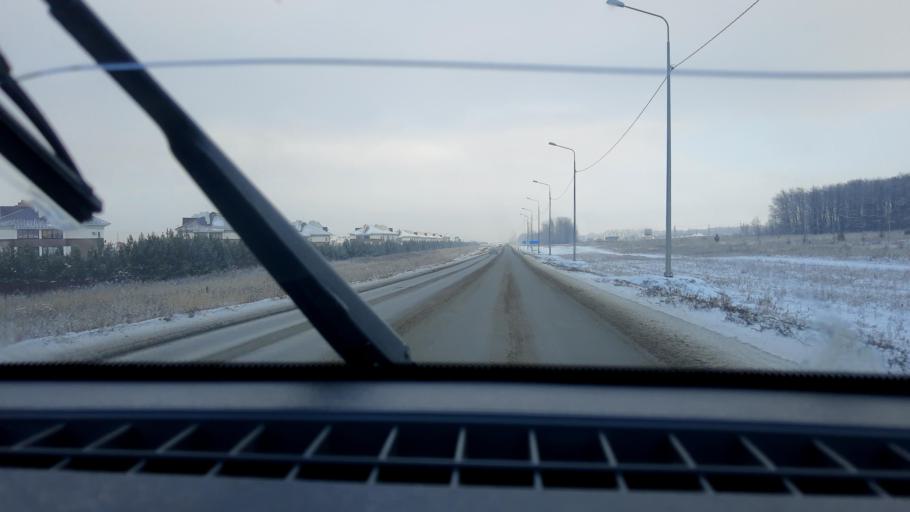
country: RU
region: Bashkortostan
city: Avdon
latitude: 54.4765
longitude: 55.8798
